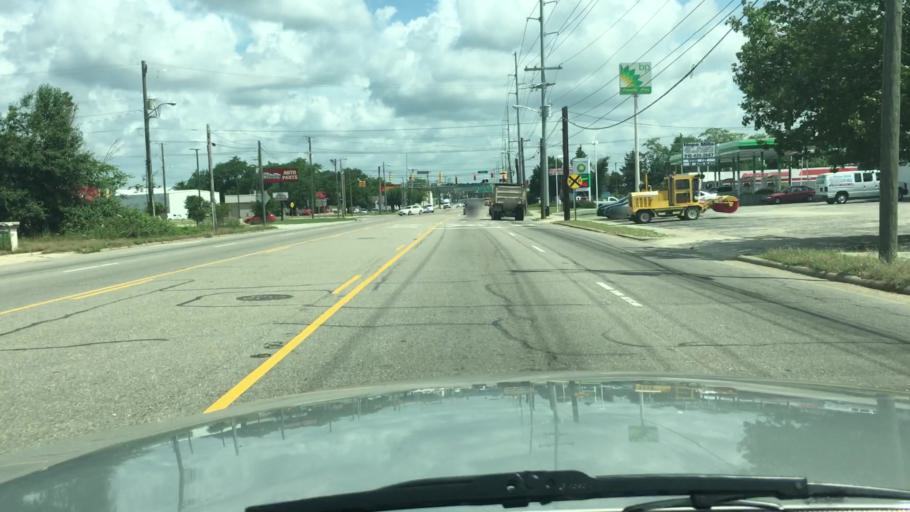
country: US
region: North Carolina
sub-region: Cumberland County
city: Fayetteville
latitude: 35.0446
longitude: -78.8657
